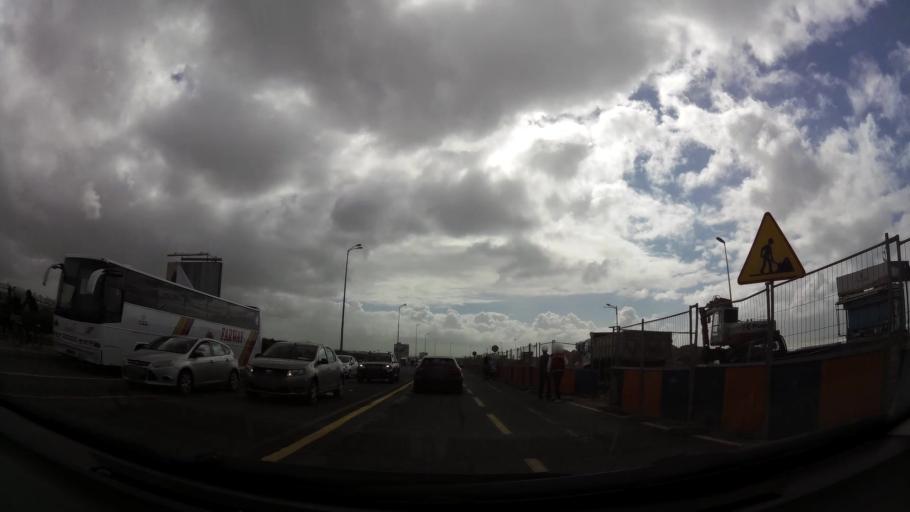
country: MA
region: Grand Casablanca
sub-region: Casablanca
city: Casablanca
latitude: 33.5846
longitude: -7.6898
